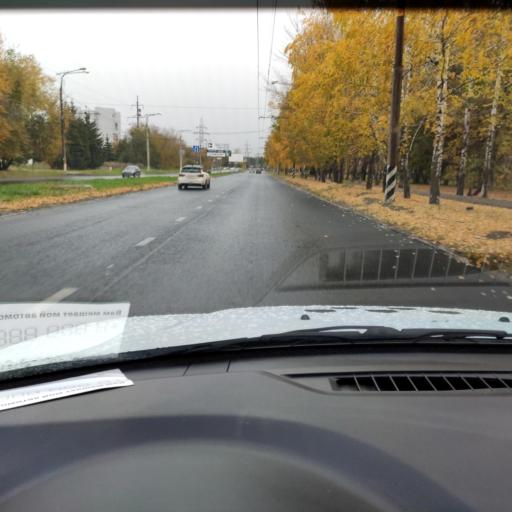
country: RU
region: Samara
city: Tol'yatti
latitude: 53.5138
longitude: 49.4475
